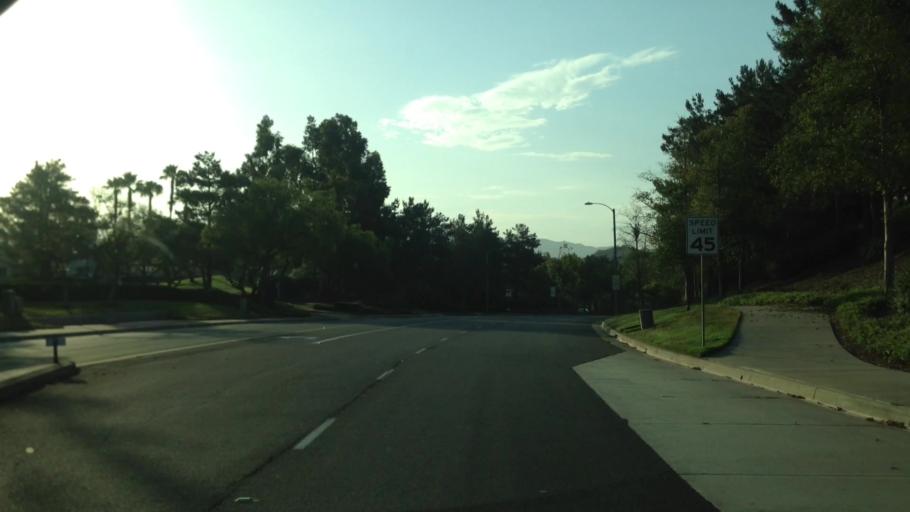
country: US
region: California
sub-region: Orange County
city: Rancho Santa Margarita
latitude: 33.6586
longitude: -117.6188
